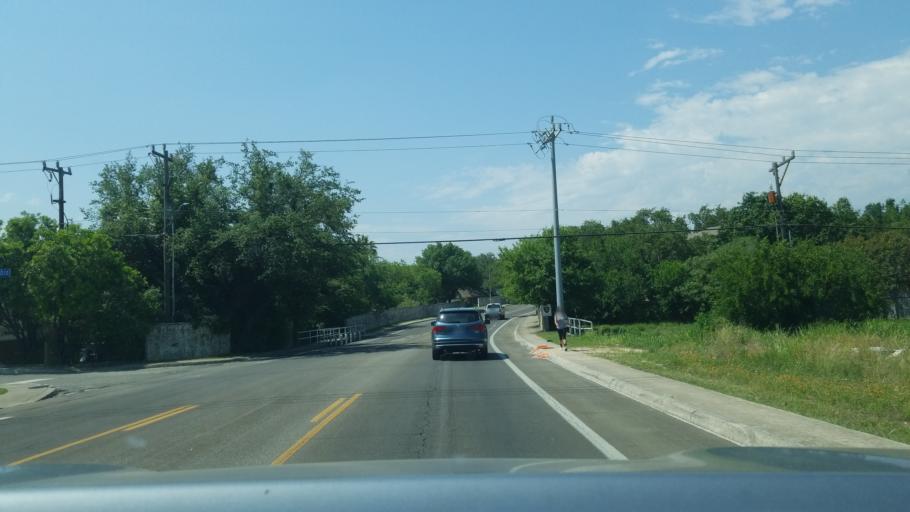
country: US
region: Texas
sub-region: Bexar County
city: Hollywood Park
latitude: 29.6329
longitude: -98.4445
